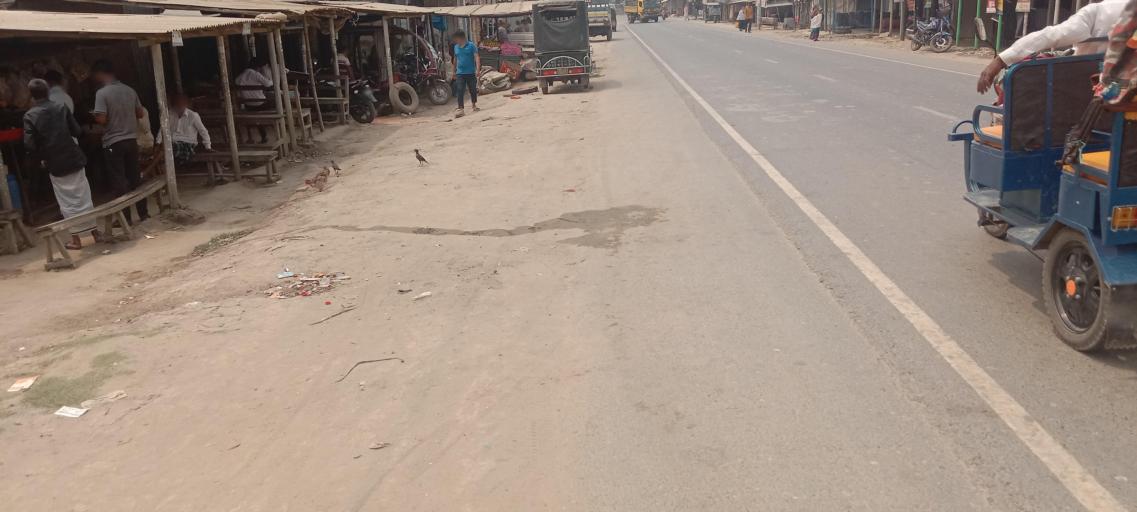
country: BD
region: Dhaka
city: Gafargaon
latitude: 24.4146
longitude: 90.4354
